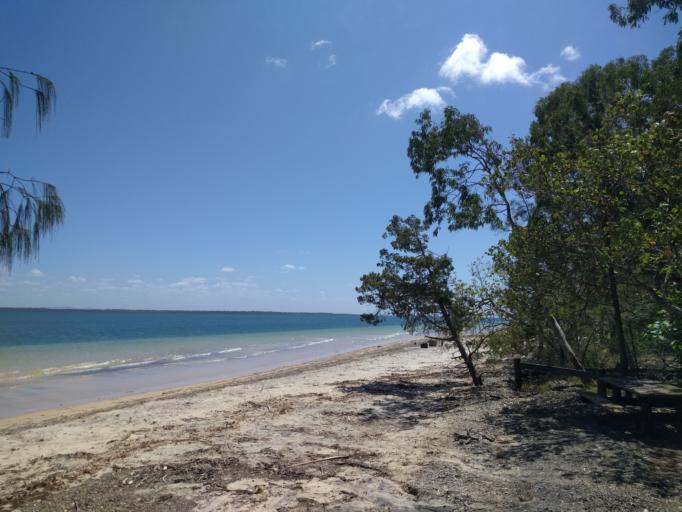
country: AU
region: Queensland
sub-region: Gympie Regional Council
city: Tin Can Bay
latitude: -25.7859
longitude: 153.0294
